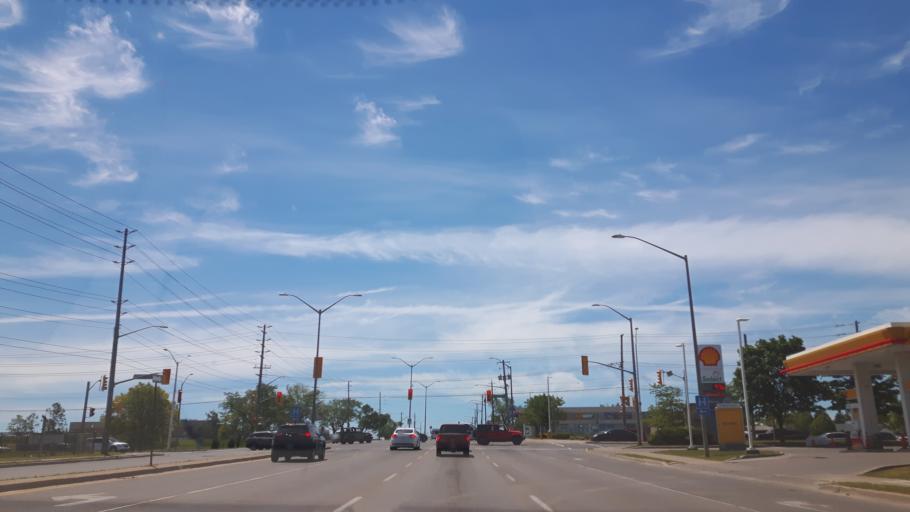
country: CA
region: Ontario
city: London
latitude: 42.9589
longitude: -81.2305
